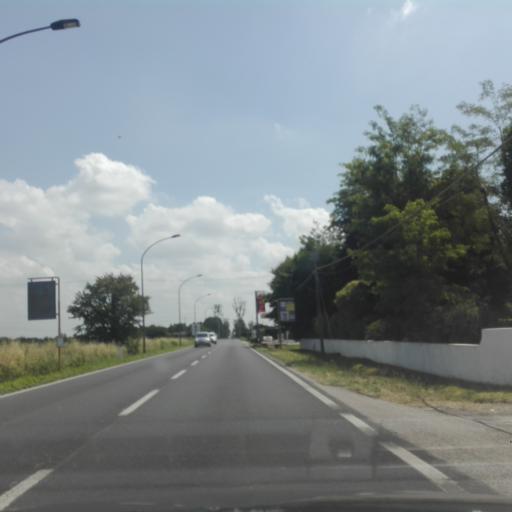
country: IT
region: Veneto
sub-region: Provincia di Rovigo
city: Buso
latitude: 45.0757
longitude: 11.8250
